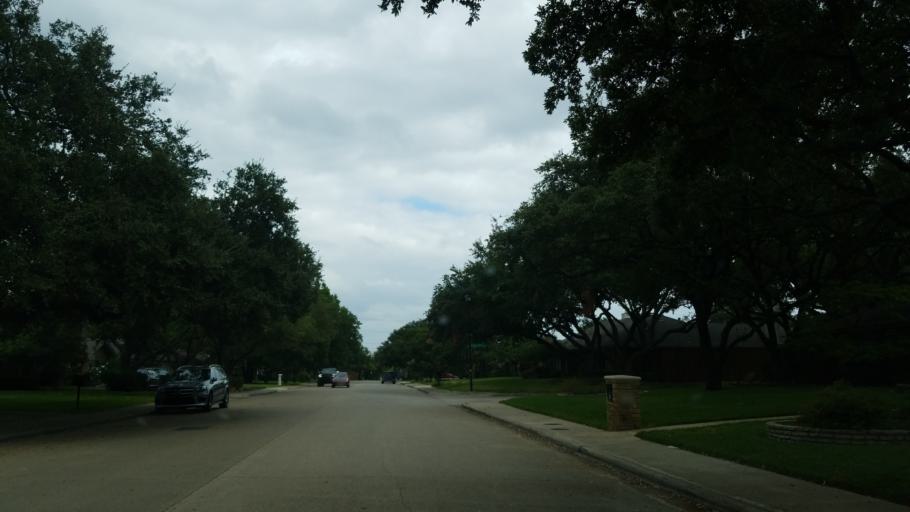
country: US
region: Texas
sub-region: Dallas County
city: Richardson
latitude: 32.9459
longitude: -96.7739
